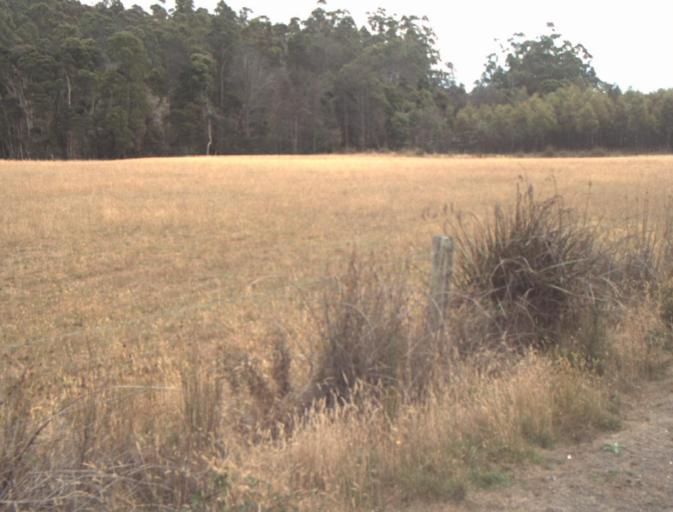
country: AU
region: Tasmania
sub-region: Launceston
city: Mayfield
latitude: -41.1901
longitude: 147.1674
